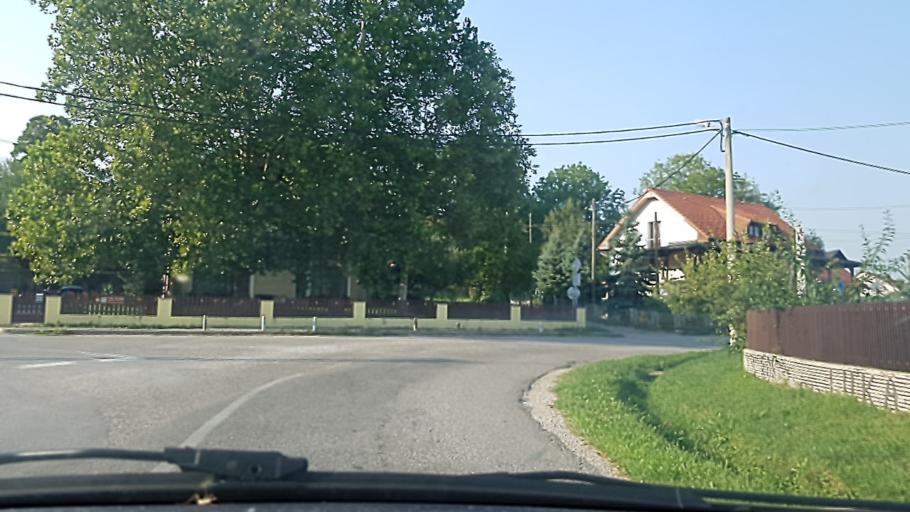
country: HR
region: Zagrebacka
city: Jakovlje
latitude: 45.9529
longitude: 15.8124
